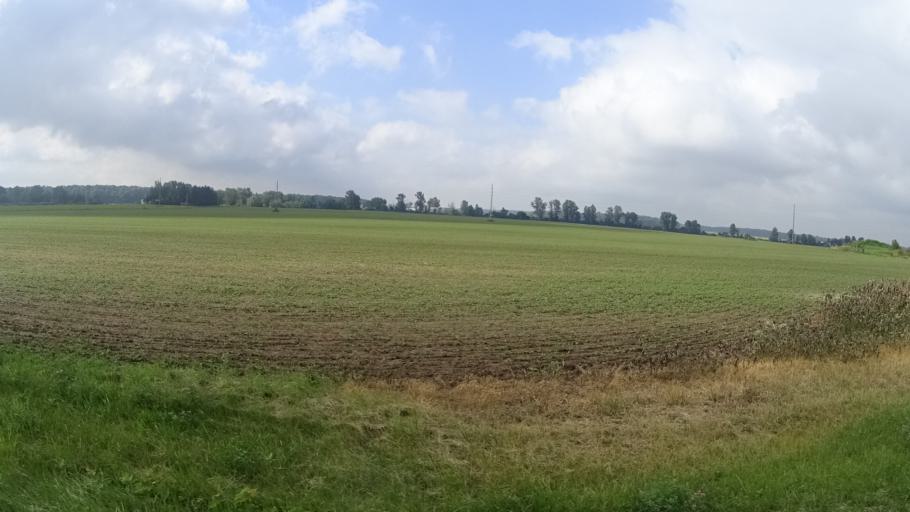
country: US
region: Ohio
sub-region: Huron County
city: Wakeman
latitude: 41.2839
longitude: -82.4449
